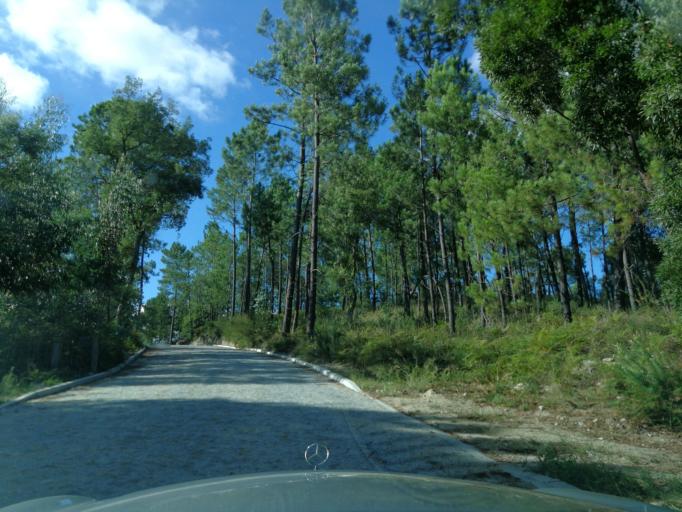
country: PT
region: Braga
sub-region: Braga
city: Adaufe
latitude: 41.5747
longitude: -8.3813
